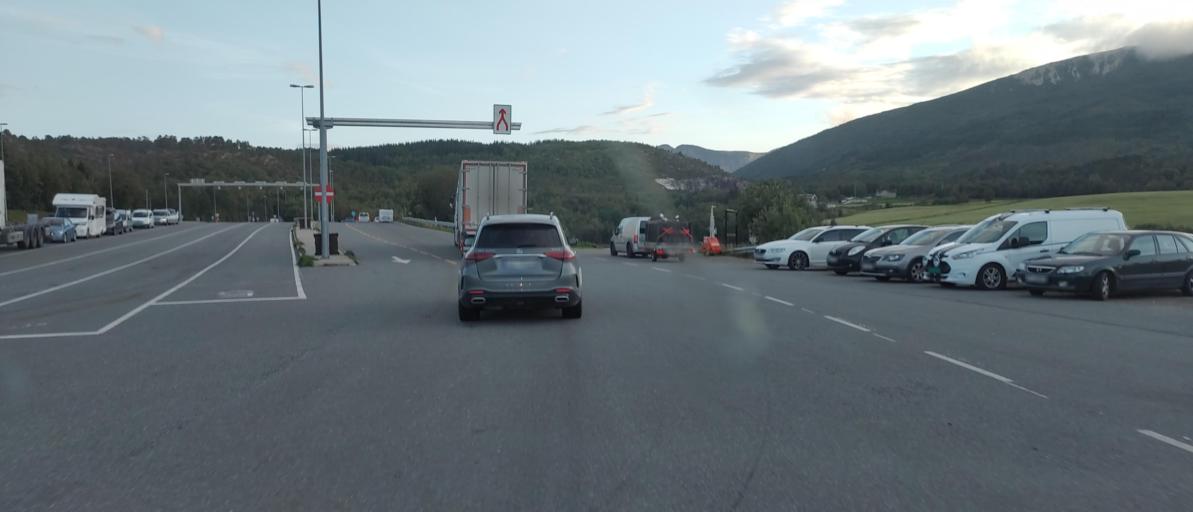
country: NO
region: Nordland
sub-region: Lodingen
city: Lodingen
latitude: 68.2235
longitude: 16.0722
